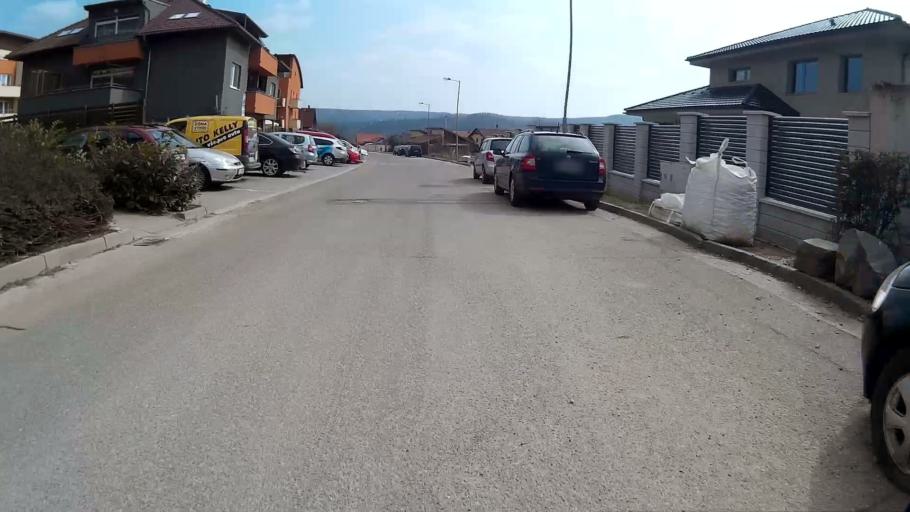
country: CZ
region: South Moravian
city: Bilovice nad Svitavou
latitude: 49.2445
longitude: 16.6561
